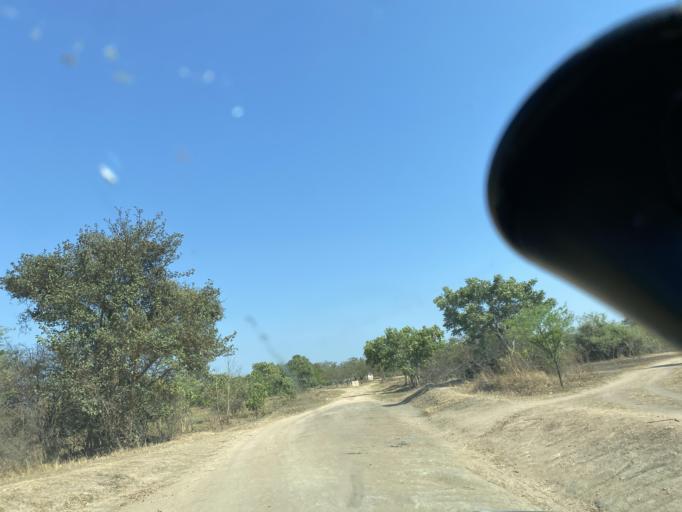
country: ZM
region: Lusaka
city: Chongwe
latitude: -15.2167
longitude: 28.8372
